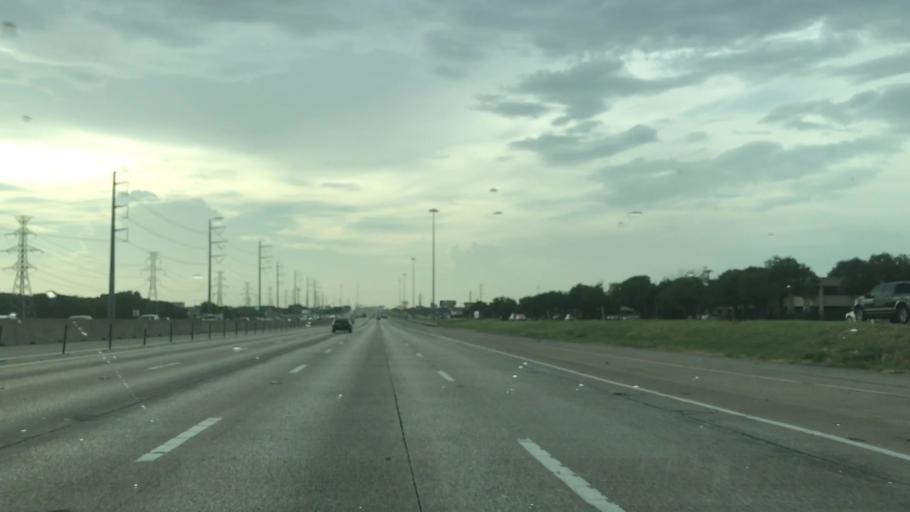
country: US
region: Texas
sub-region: Dallas County
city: Garland
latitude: 32.8582
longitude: -96.6518
